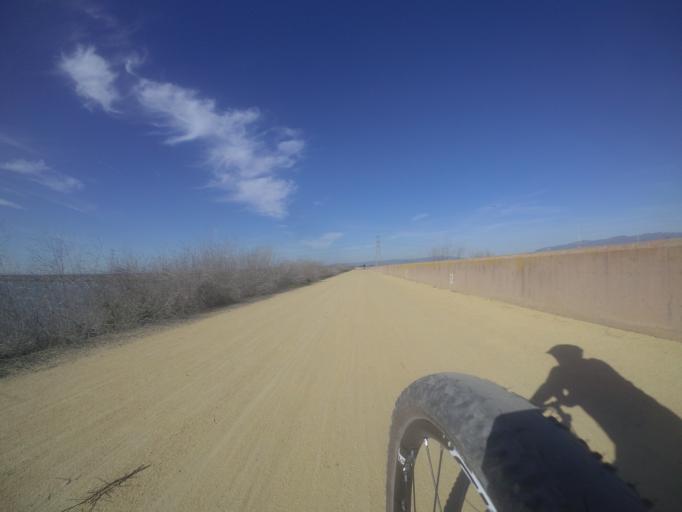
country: US
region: California
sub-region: Santa Clara County
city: Sunnyvale
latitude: 37.4158
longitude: -121.9871
